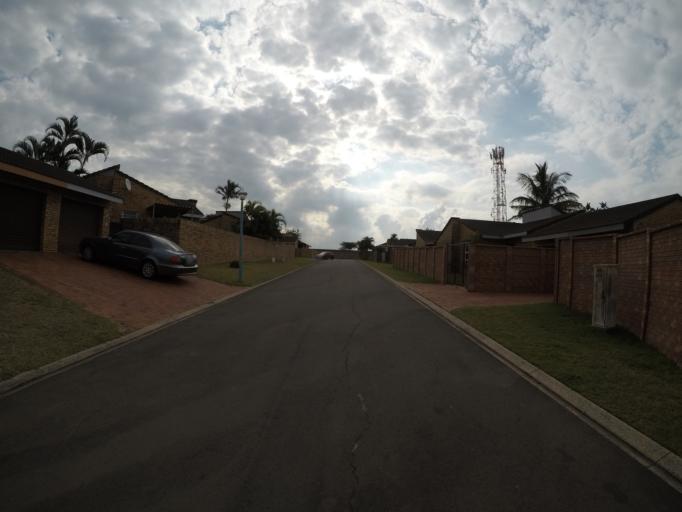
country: ZA
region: KwaZulu-Natal
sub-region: uThungulu District Municipality
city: Richards Bay
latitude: -28.7376
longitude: 32.0842
